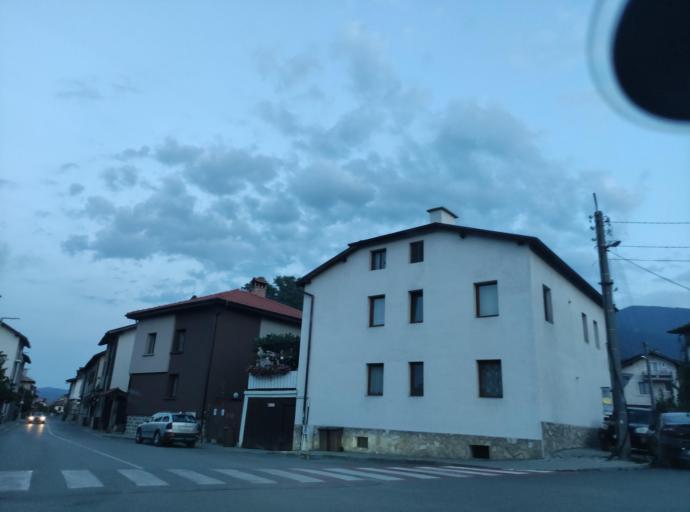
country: BG
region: Blagoevgrad
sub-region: Obshtina Bansko
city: Bansko
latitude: 41.8339
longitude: 23.4873
